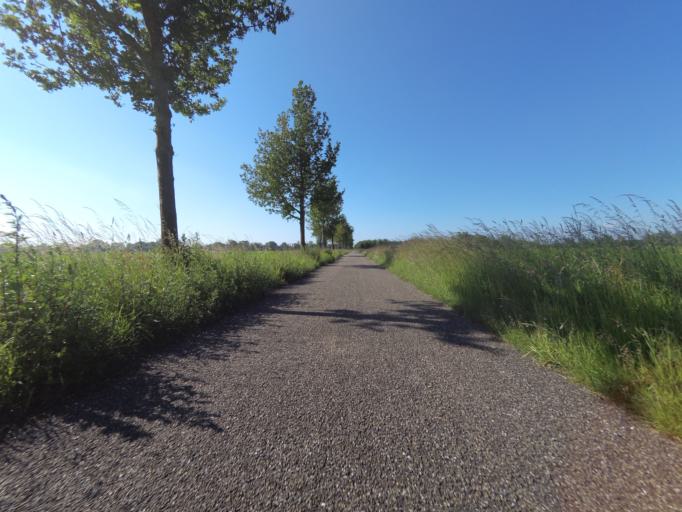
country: NL
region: Gelderland
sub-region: Gemeente Voorst
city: Voorst
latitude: 52.1667
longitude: 6.1032
